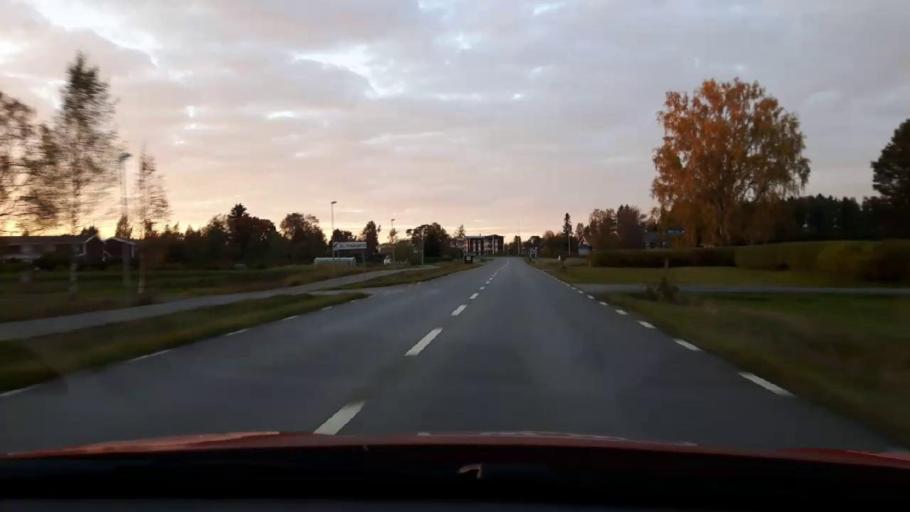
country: SE
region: Jaemtland
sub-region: OEstersunds Kommun
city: Ostersund
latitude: 63.2430
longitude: 14.5732
